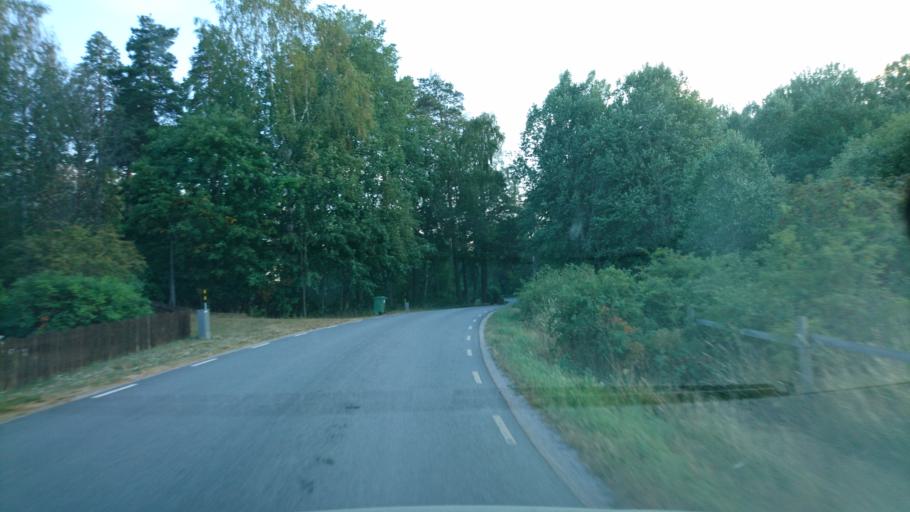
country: SE
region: Uppsala
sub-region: Uppsala Kommun
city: Saevja
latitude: 59.8107
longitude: 17.6798
